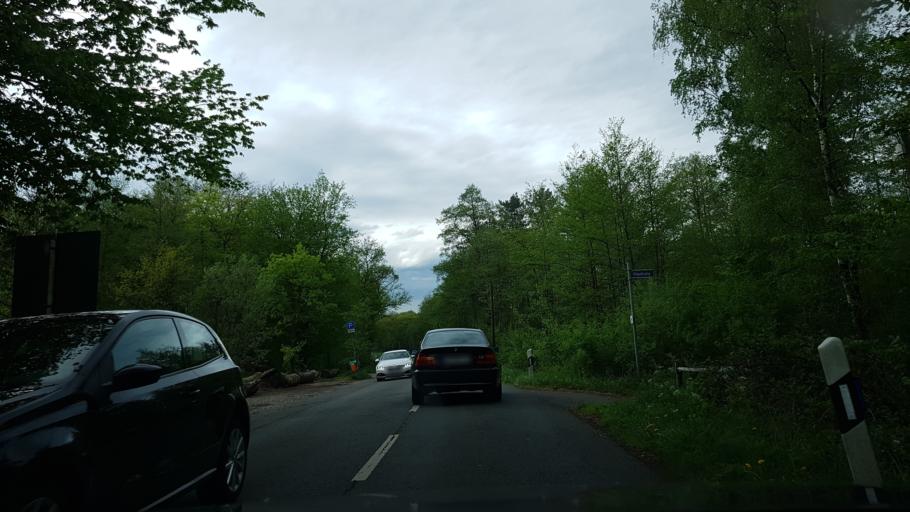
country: DE
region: North Rhine-Westphalia
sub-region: Regierungsbezirk Dusseldorf
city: Muelheim (Ruhr)
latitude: 51.3831
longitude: 6.8458
